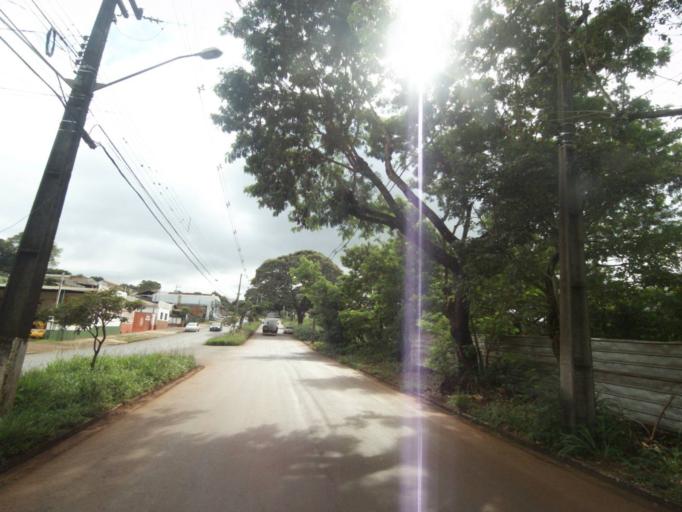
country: BR
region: Parana
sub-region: Campo Mourao
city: Campo Mourao
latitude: -24.0525
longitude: -52.3812
